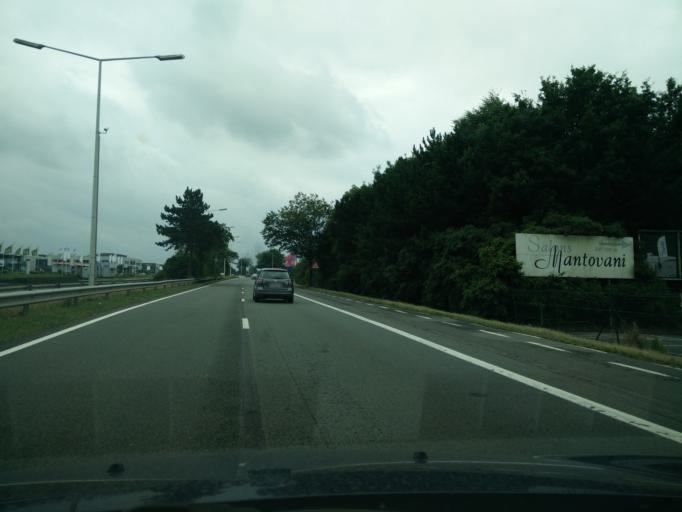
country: BE
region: Flanders
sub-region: Provincie Oost-Vlaanderen
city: Oudenaarde
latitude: 50.8701
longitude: 3.6074
